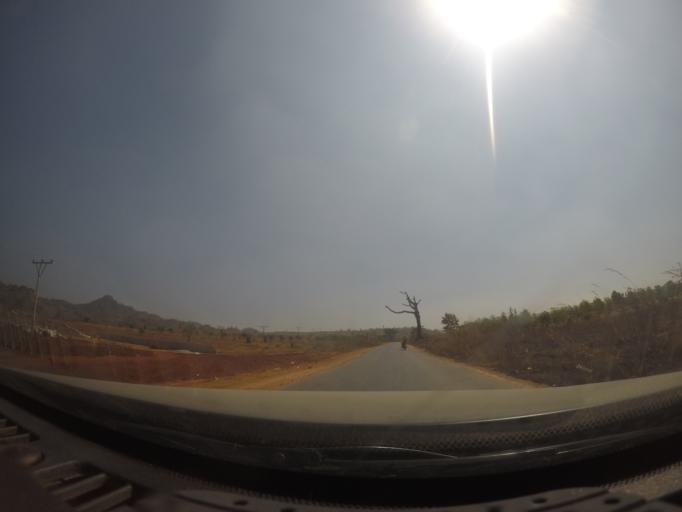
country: MM
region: Shan
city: Taunggyi
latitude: 20.8104
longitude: 97.2460
